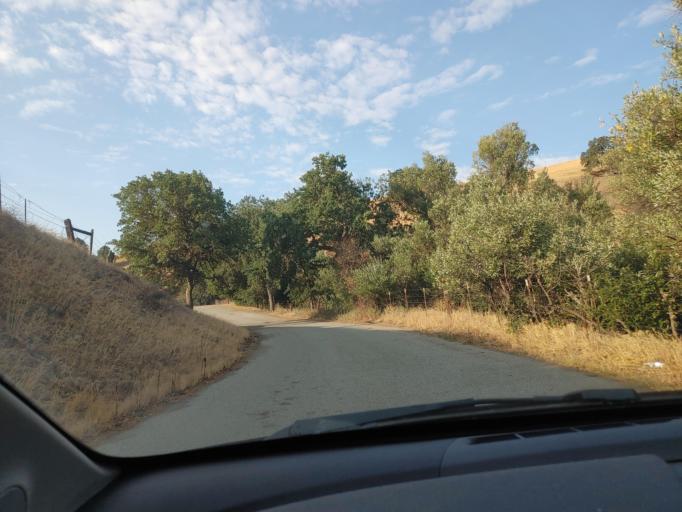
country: US
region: California
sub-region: San Benito County
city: Ridgemark
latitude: 36.7491
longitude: -121.1584
